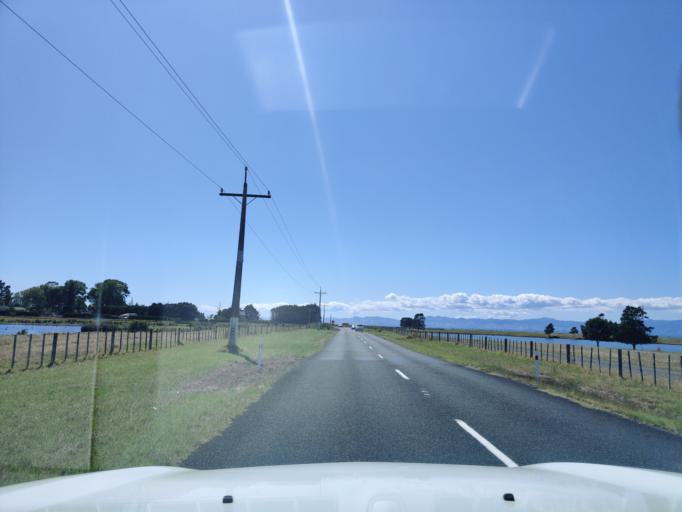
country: NZ
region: Waikato
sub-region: Thames-Coromandel District
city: Thames
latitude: -37.0571
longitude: 175.3004
